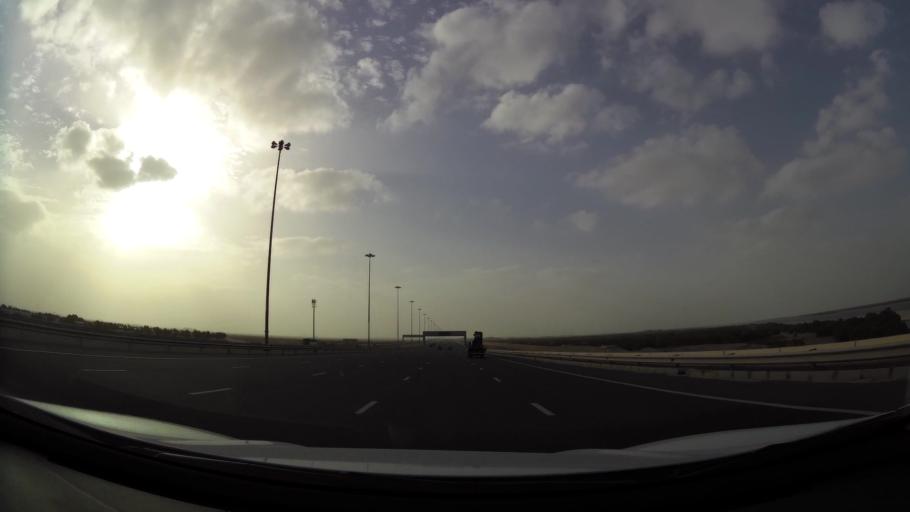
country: AE
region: Abu Dhabi
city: Abu Dhabi
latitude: 24.5232
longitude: 54.5138
